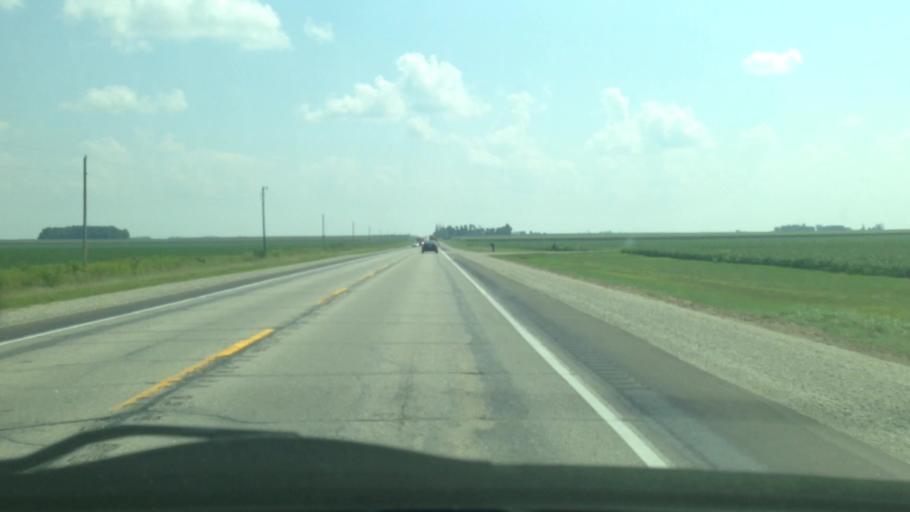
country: US
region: Iowa
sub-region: Howard County
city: Cresco
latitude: 43.4202
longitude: -92.2987
